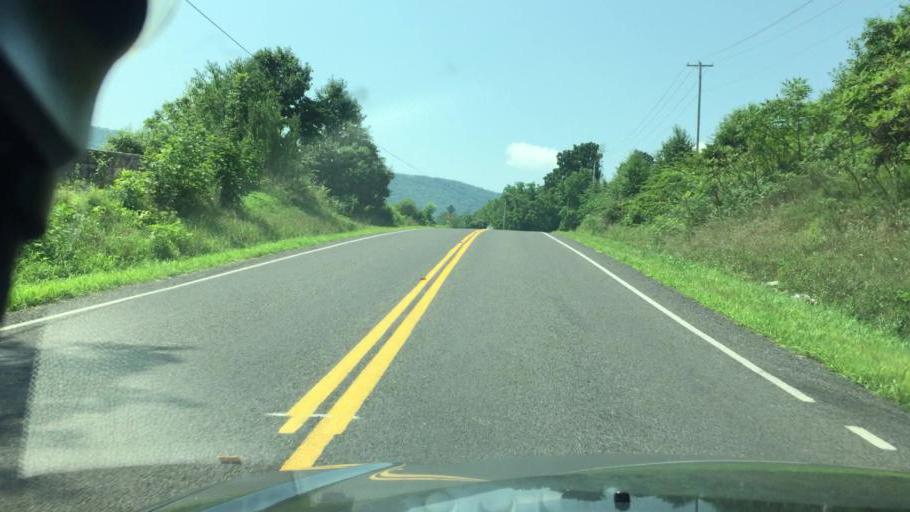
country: US
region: Pennsylvania
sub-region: Columbia County
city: Mifflinville
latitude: 40.9997
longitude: -76.3245
